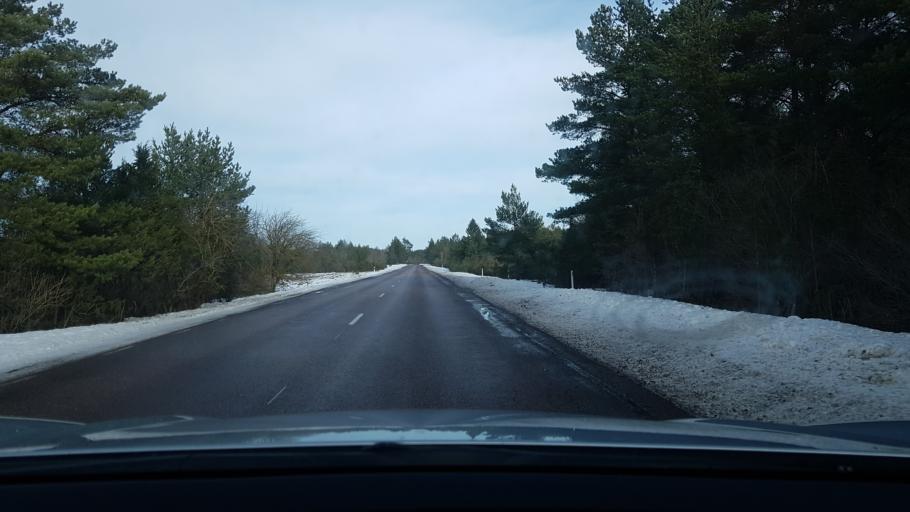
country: EE
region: Saare
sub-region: Kuressaare linn
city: Kuressaare
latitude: 58.3347
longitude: 22.5669
